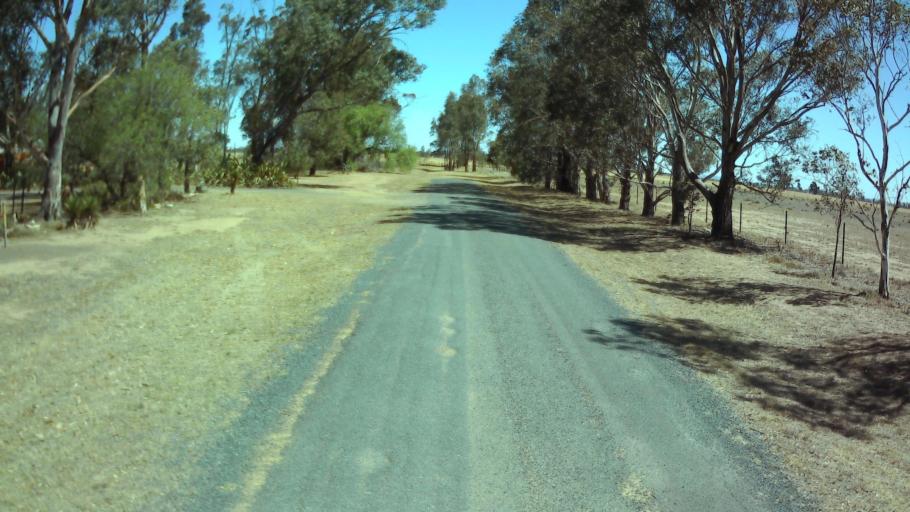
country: AU
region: New South Wales
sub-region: Weddin
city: Grenfell
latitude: -34.0153
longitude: 147.7897
